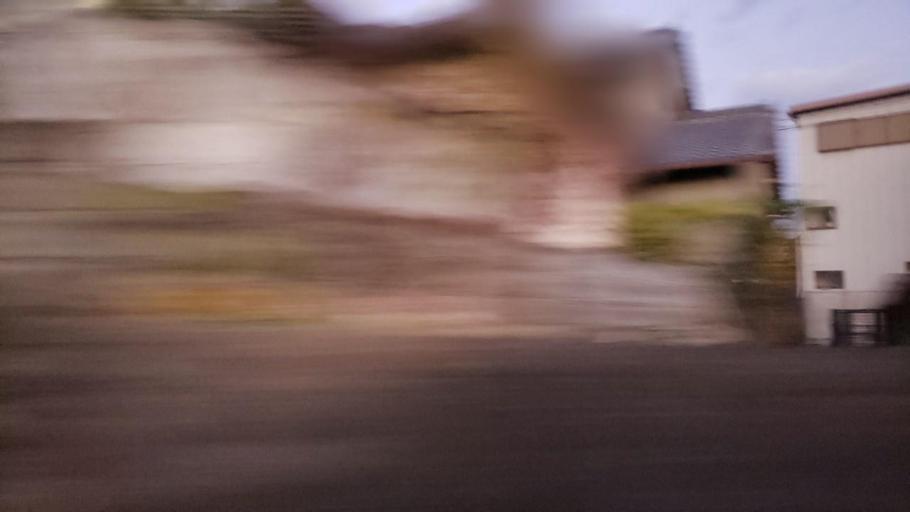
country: JP
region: Tokushima
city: Kamojimacho-jogejima
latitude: 34.0910
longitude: 134.2846
